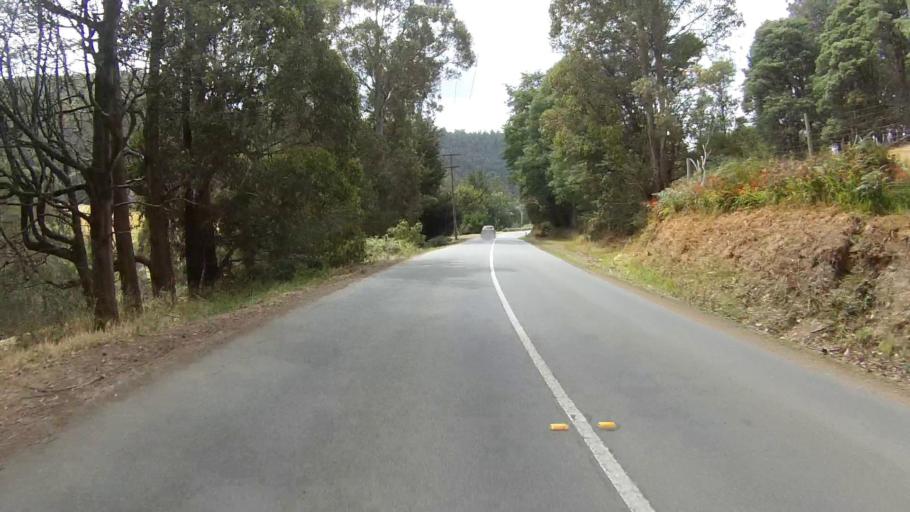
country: AU
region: Tasmania
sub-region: Kingborough
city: Kettering
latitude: -43.1071
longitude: 147.2024
